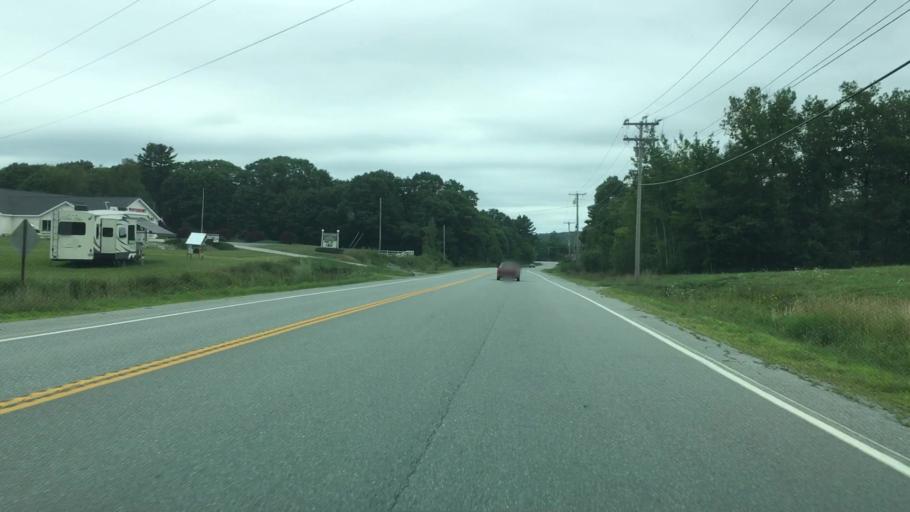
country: US
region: Maine
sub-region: Waldo County
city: Frankfort
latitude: 44.6145
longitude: -68.8694
